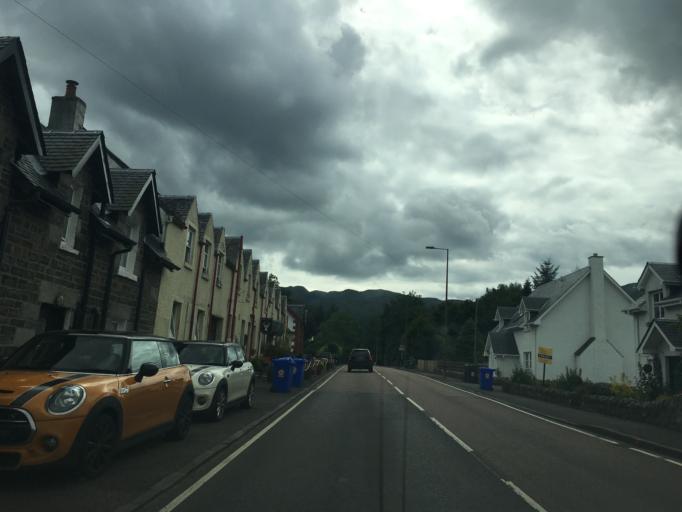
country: GB
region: Scotland
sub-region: Stirling
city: Callander
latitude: 56.3237
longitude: -4.3286
